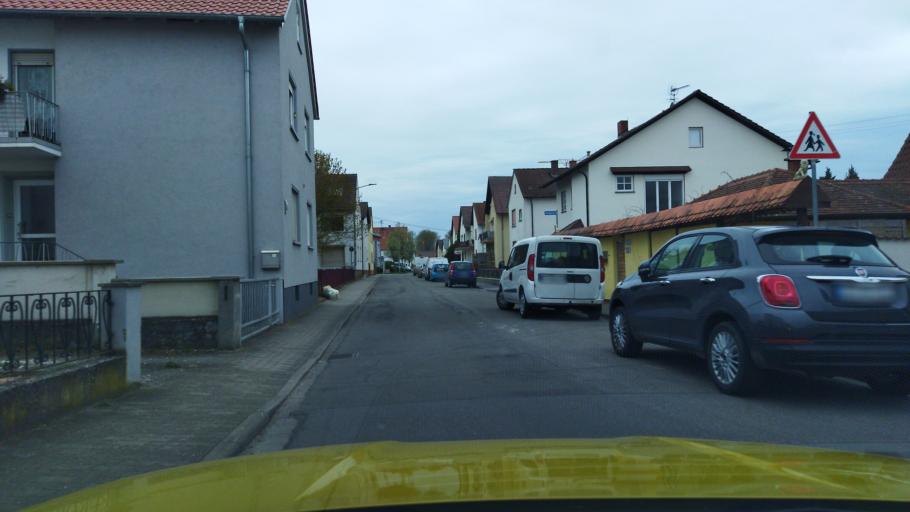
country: DE
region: Rheinland-Pfalz
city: Hanhofen
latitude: 49.3143
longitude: 8.3461
